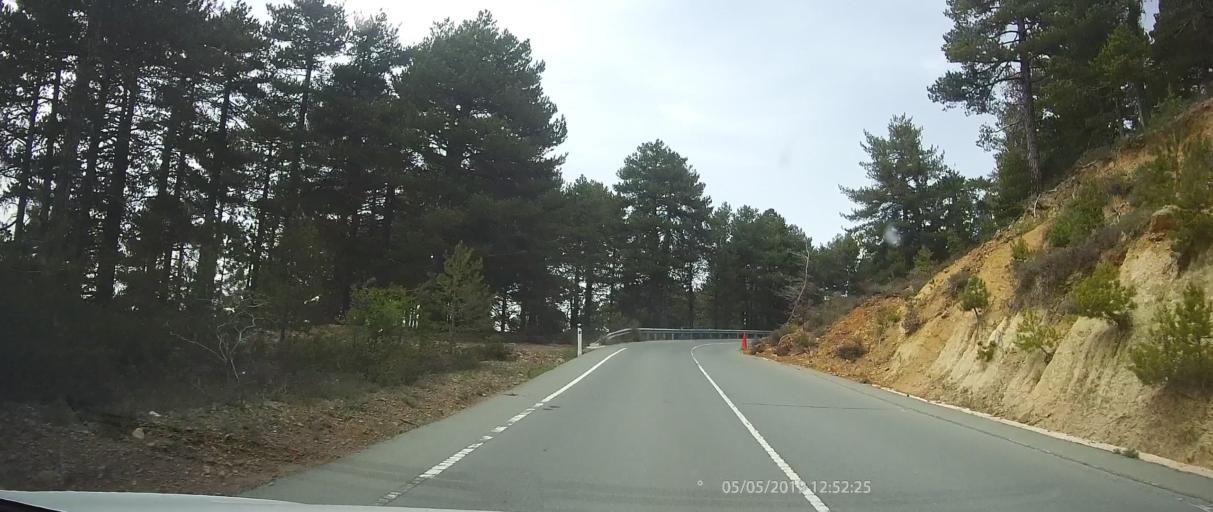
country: CY
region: Lefkosia
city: Kakopetria
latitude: 34.9508
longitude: 32.8369
